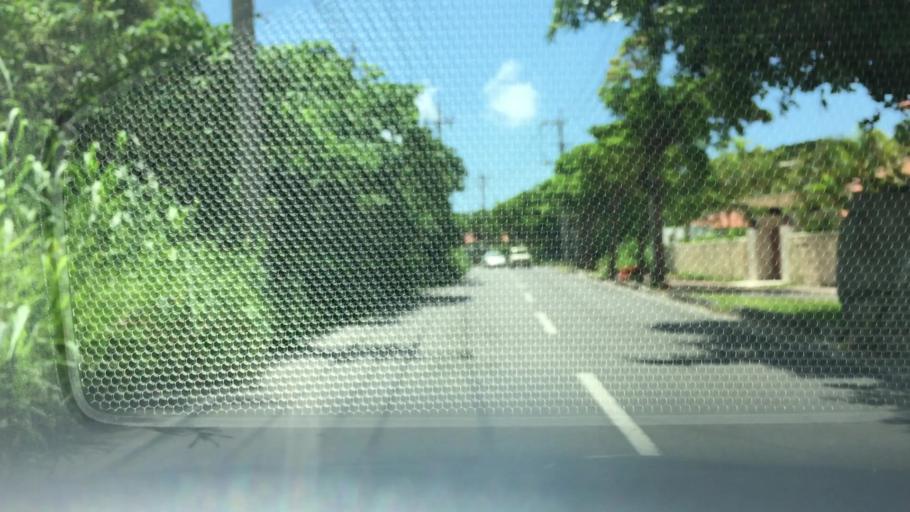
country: JP
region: Okinawa
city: Ishigaki
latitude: 24.3632
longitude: 124.1164
